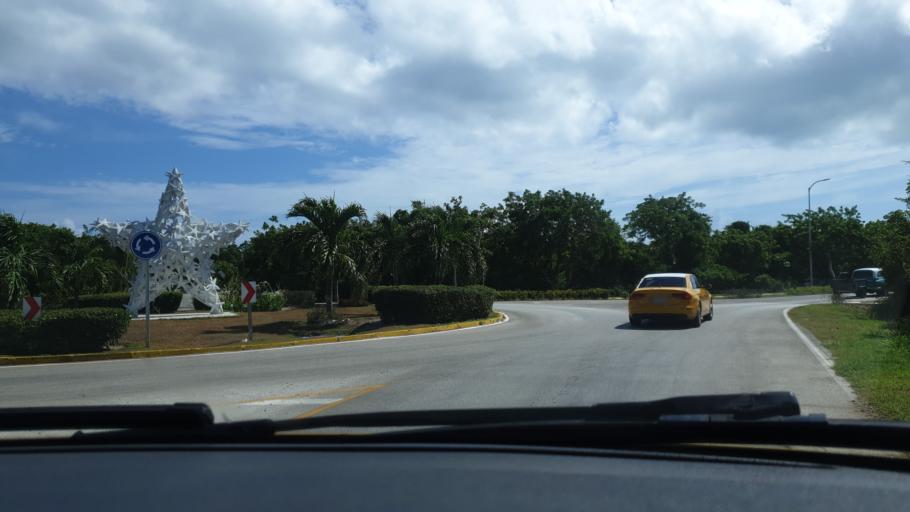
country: CU
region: Sancti Spiritus
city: Yaguajay
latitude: 22.6557
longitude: -79.0380
